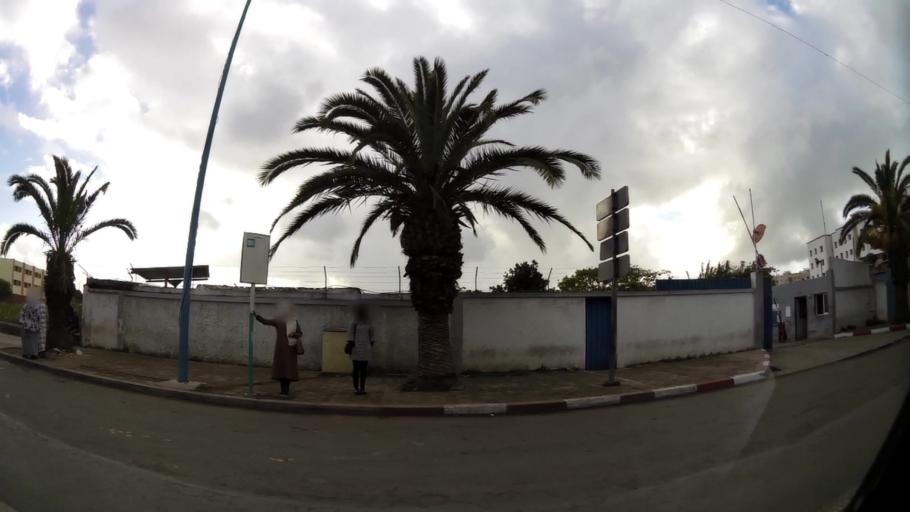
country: MA
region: Grand Casablanca
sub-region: Mohammedia
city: Mohammedia
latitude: 33.6774
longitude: -7.3964
